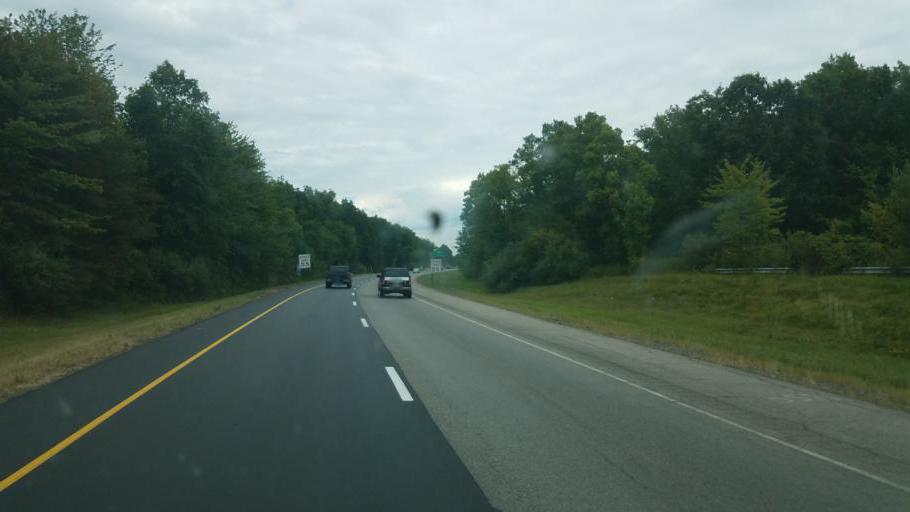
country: US
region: Ohio
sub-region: Mahoning County
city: Austintown
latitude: 41.1170
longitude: -80.7544
